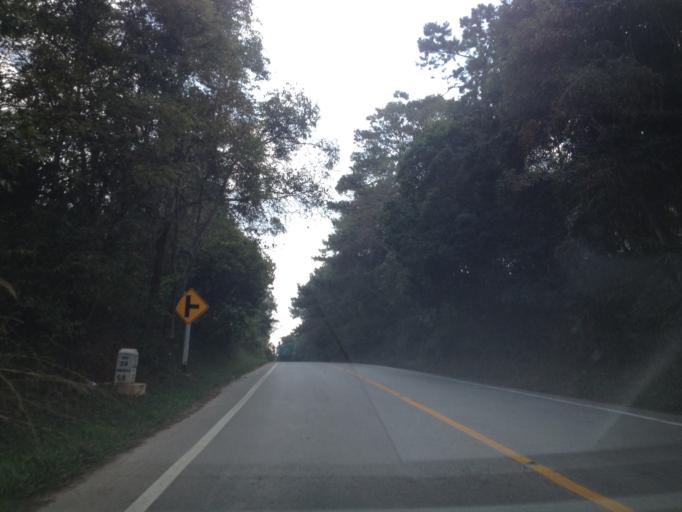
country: TH
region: Chiang Mai
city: Hot
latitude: 18.1413
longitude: 98.3697
